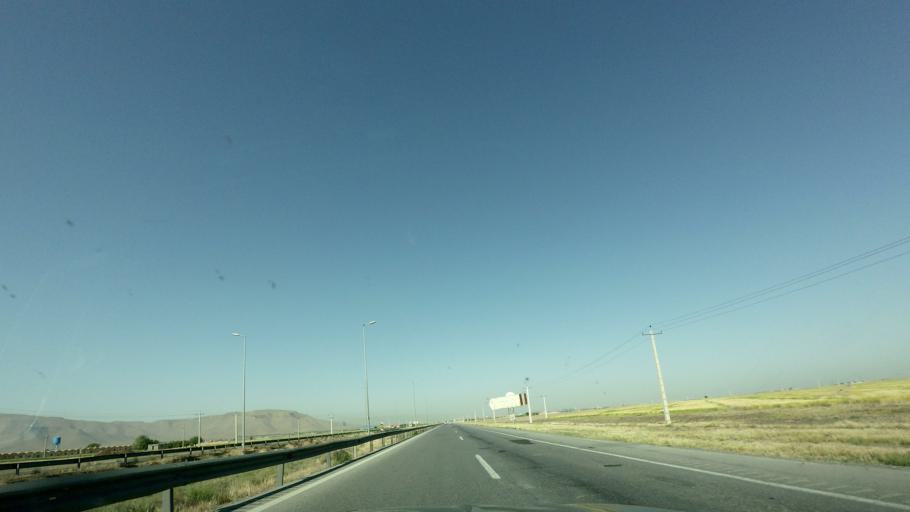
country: IR
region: Markazi
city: Arak
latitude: 34.1616
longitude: 50.0178
